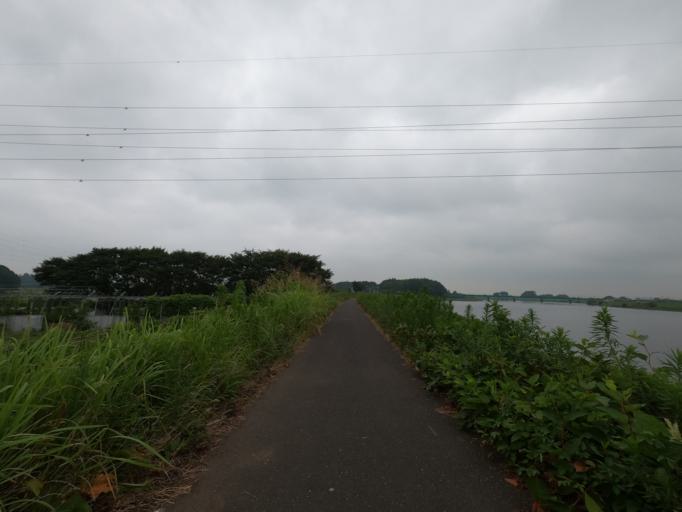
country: JP
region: Ibaraki
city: Moriya
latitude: 35.9414
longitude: 140.0281
